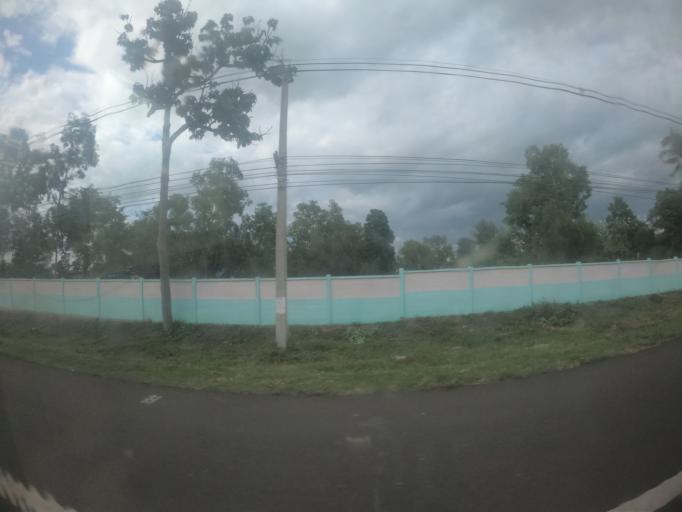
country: TH
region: Surin
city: Kap Choeng
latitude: 14.5513
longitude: 103.5089
